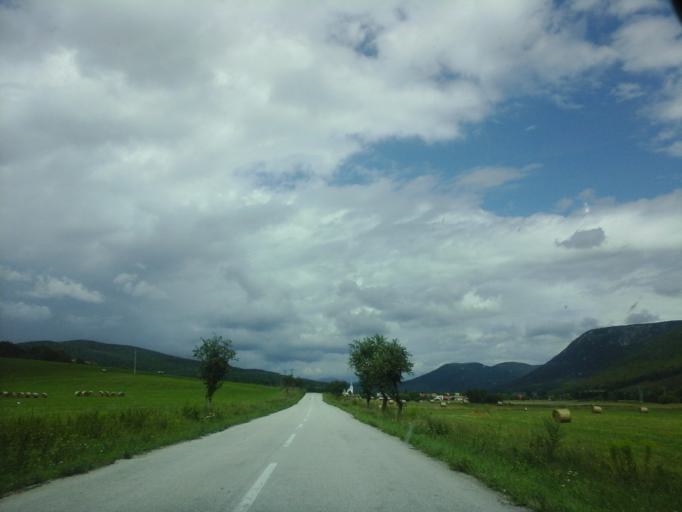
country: SK
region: Kosicky
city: Roznava
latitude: 48.5992
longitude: 20.3831
